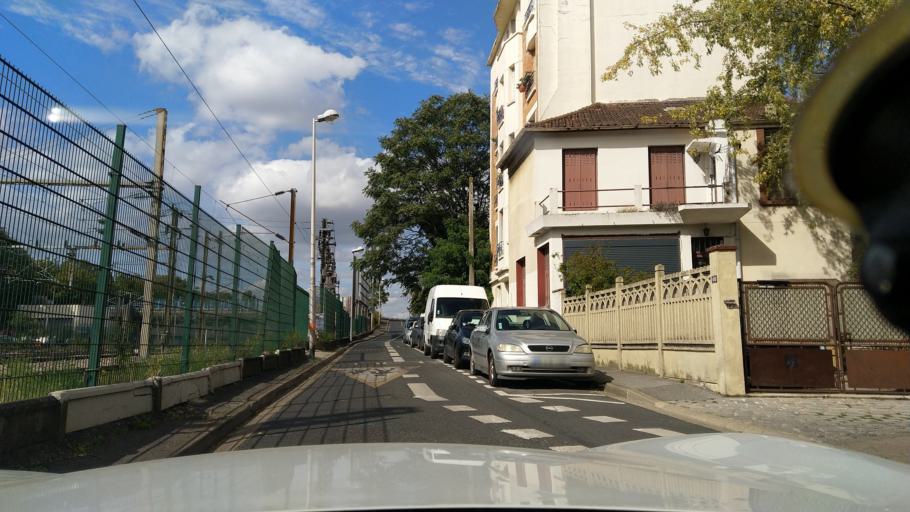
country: FR
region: Ile-de-France
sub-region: Departement du Val-de-Marne
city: Le Perreux-sur-Marne
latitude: 48.8423
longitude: 2.4937
